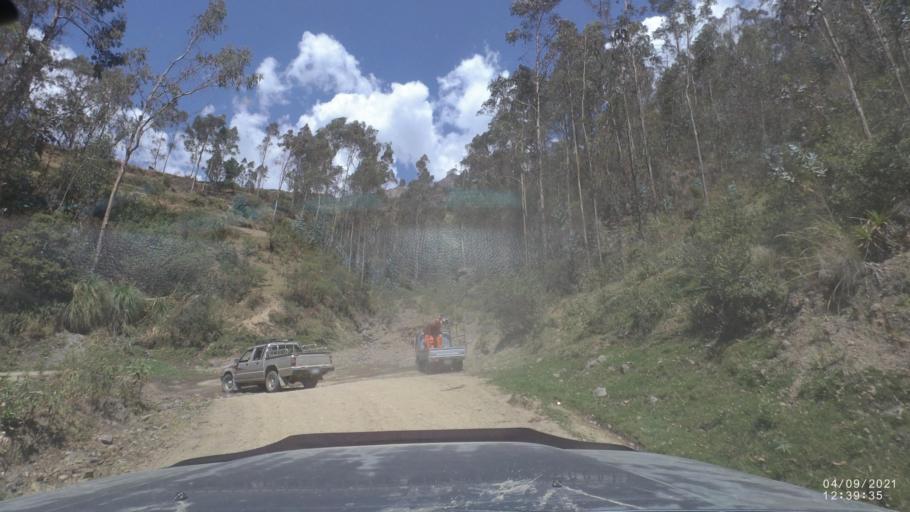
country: BO
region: Cochabamba
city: Colchani
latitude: -17.2303
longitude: -66.4988
